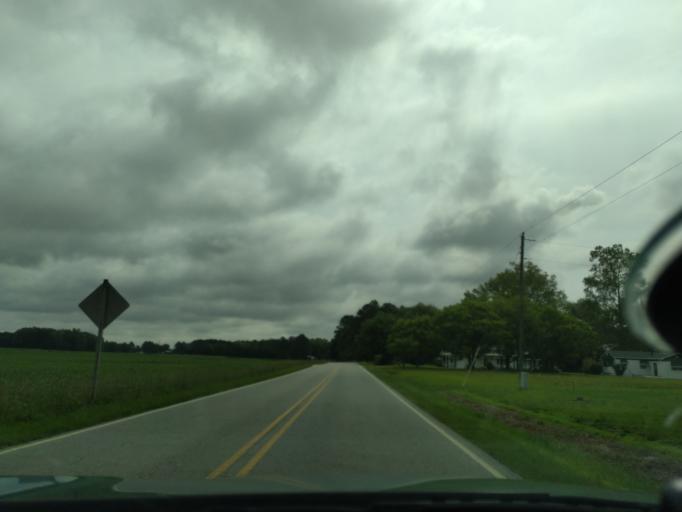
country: US
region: North Carolina
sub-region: Washington County
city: Plymouth
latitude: 35.8561
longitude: -76.7201
